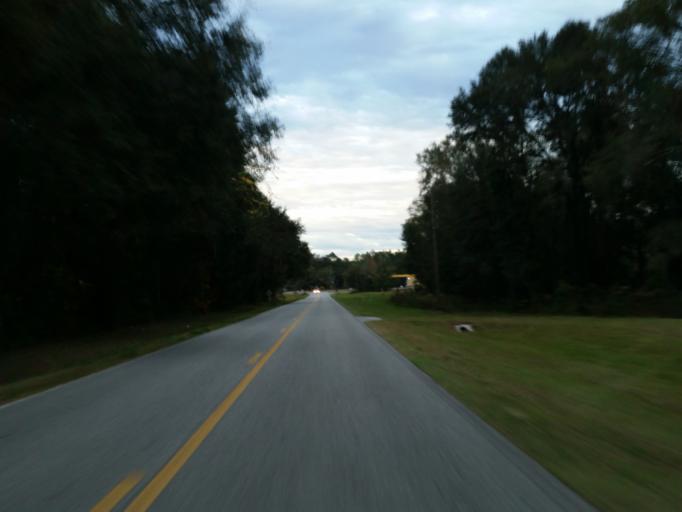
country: US
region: Florida
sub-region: Hamilton County
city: Jasper
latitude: 30.5175
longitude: -83.0638
